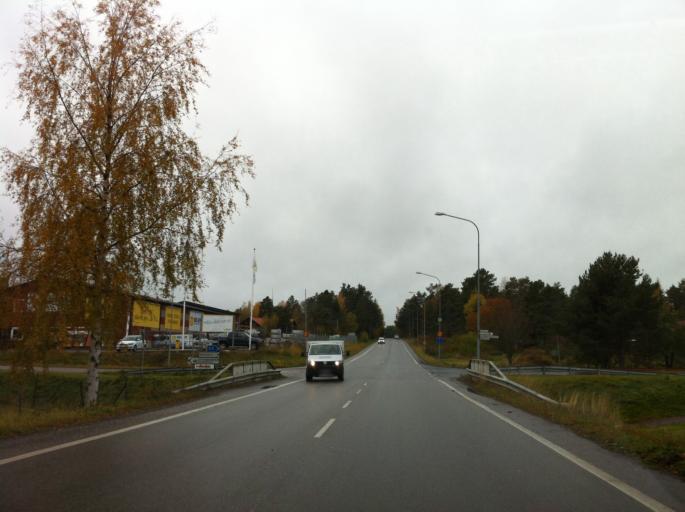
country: SE
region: Uppsala
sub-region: Osthammars Kommun
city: OEsthammar
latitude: 60.2594
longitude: 18.3580
